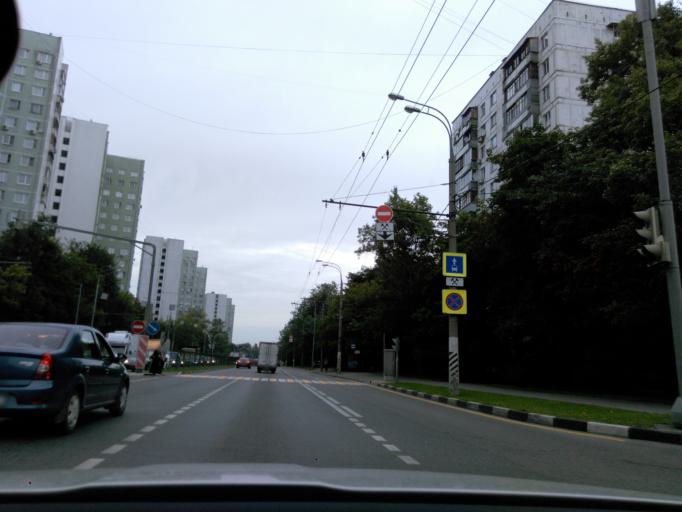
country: RU
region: Moscow
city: Tsaritsyno
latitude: 55.6229
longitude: 37.6572
